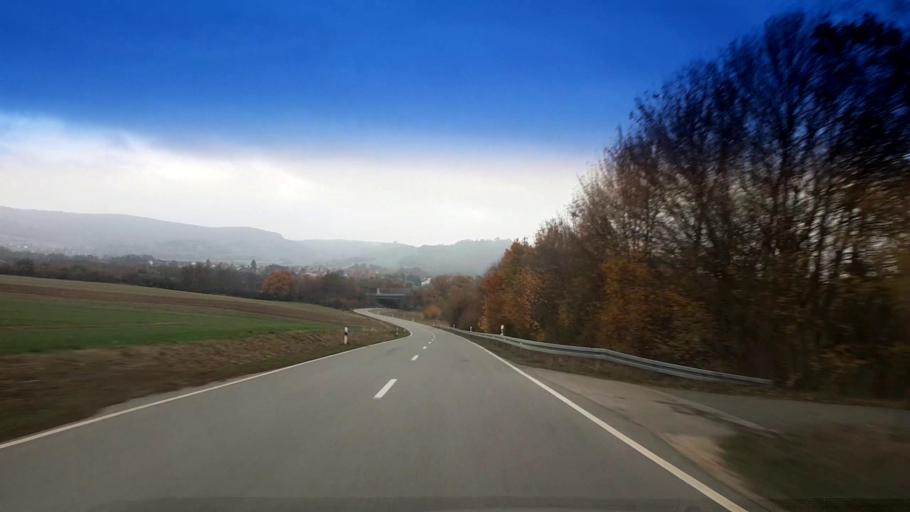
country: DE
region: Bavaria
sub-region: Upper Franconia
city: Schesslitz
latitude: 49.9851
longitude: 11.0295
